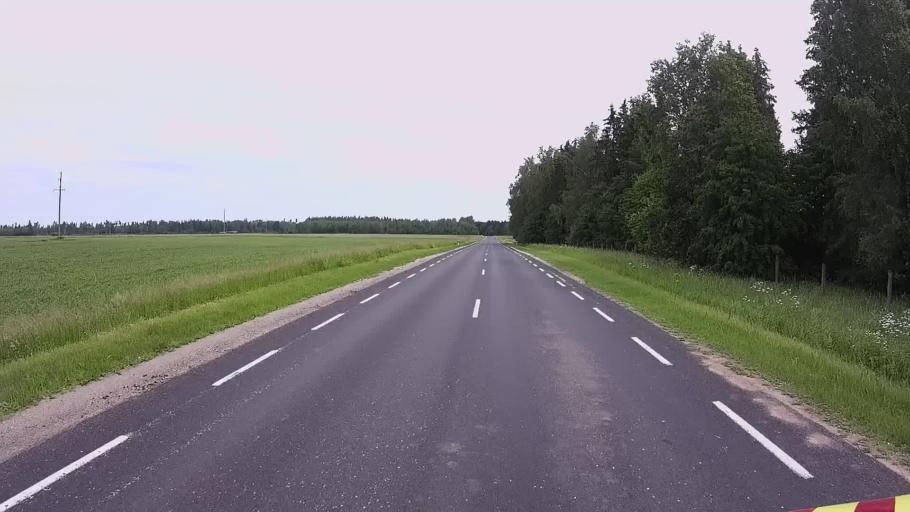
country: EE
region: Viljandimaa
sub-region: Karksi vald
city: Karksi-Nuia
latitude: 58.1978
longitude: 25.6155
